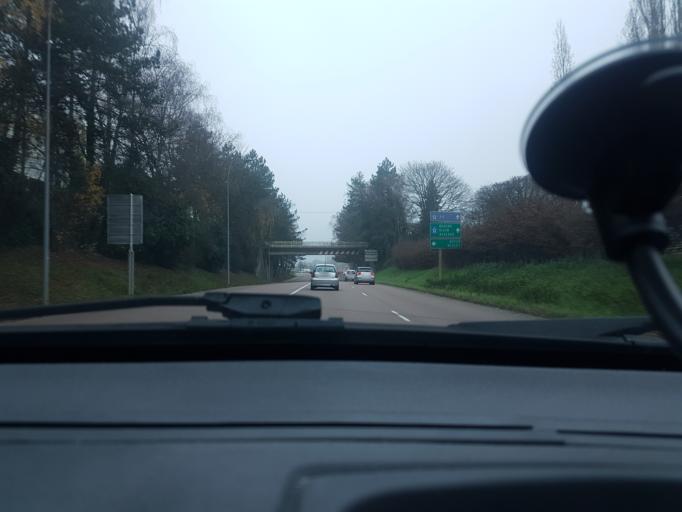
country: FR
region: Bourgogne
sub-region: Departement de Saone-et-Loire
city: Chalon-sur-Saone
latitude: 46.7936
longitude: 4.8393
